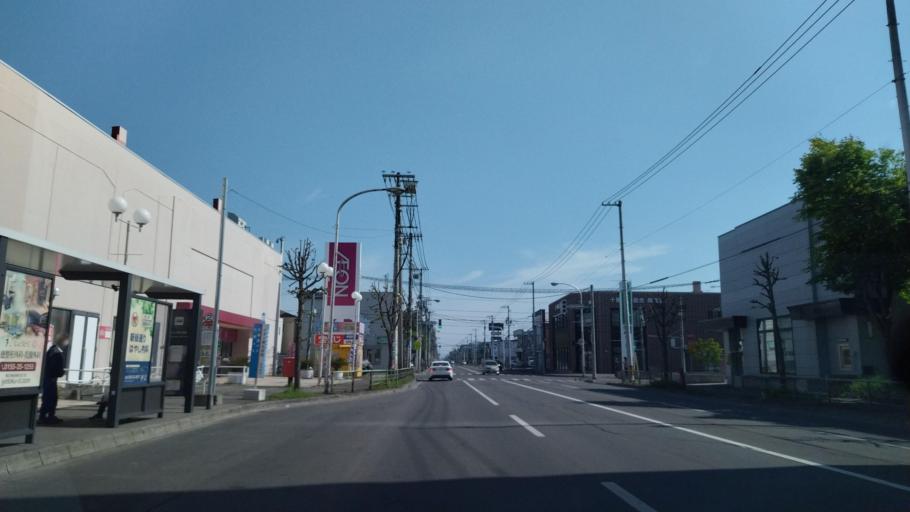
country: JP
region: Hokkaido
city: Obihiro
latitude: 42.9088
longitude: 143.1992
